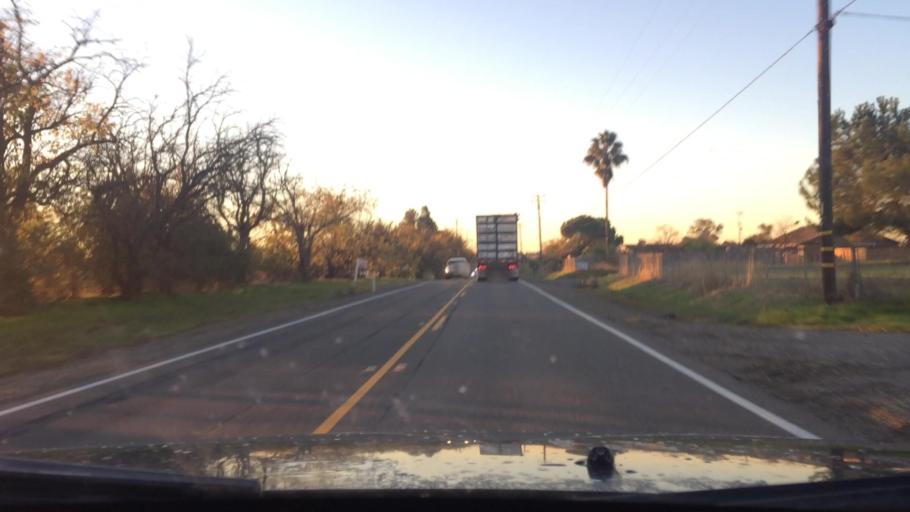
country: US
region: California
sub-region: Sacramento County
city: Vineyard
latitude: 38.5136
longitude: -121.2980
